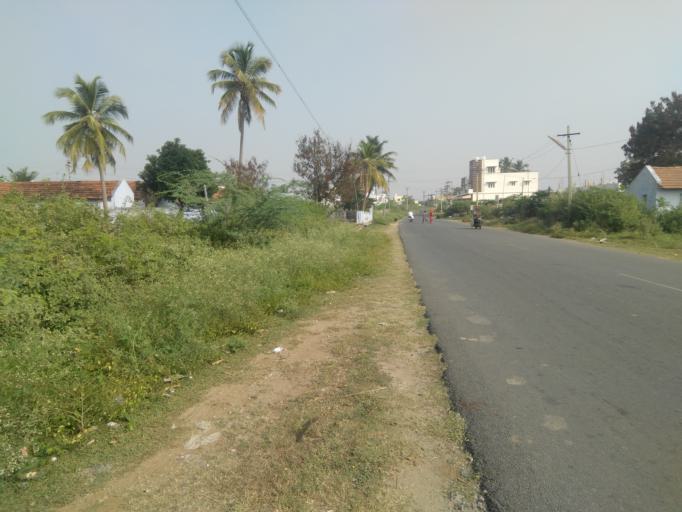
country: IN
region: Tamil Nadu
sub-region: Coimbatore
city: Karamadai
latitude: 11.2500
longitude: 76.9613
